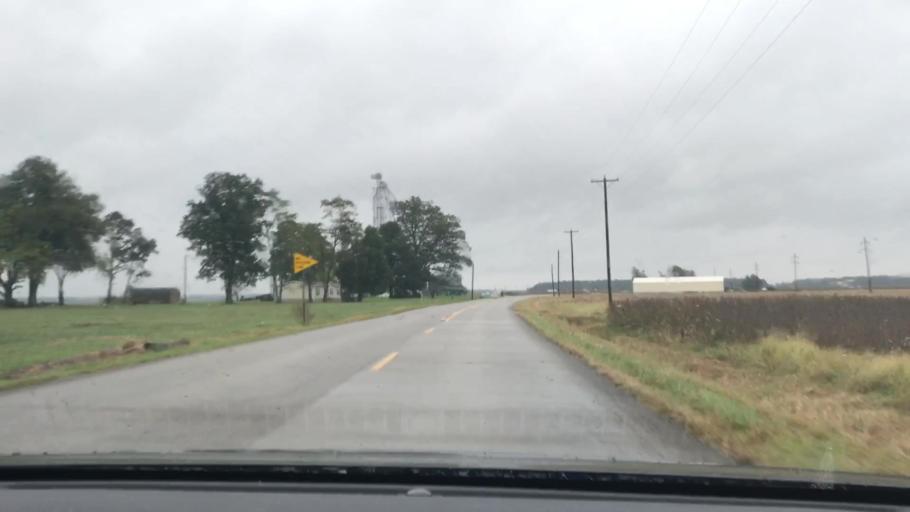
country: US
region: Kentucky
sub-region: McLean County
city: Calhoun
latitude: 37.5273
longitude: -87.3495
